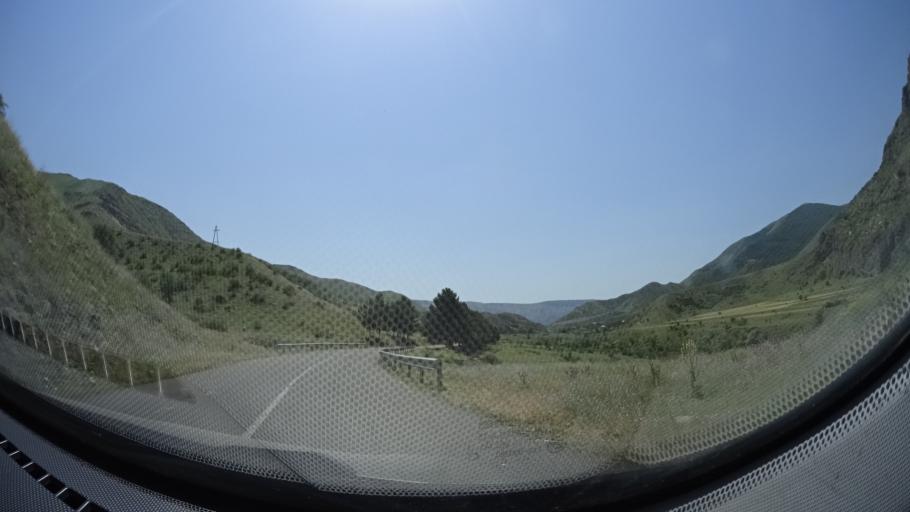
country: GE
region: Samtskhe-Javakheti
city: Aspindza
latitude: 41.4481
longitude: 43.3069
